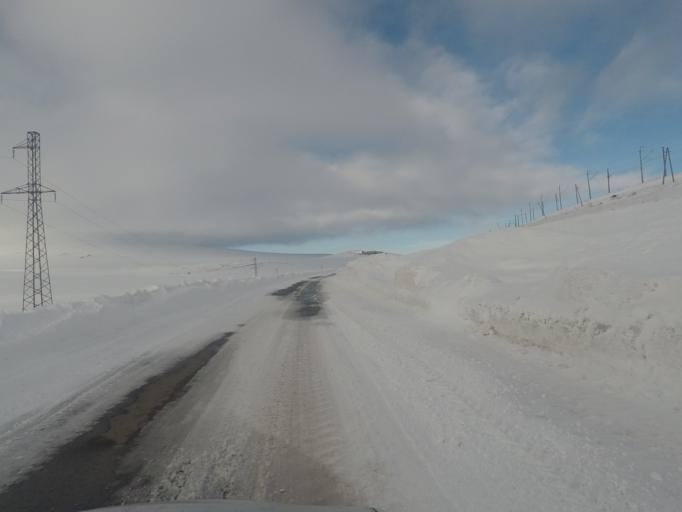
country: GE
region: Kvemo Kartli
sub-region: Tsalka
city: Tsalka
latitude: 41.4797
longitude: 43.8507
